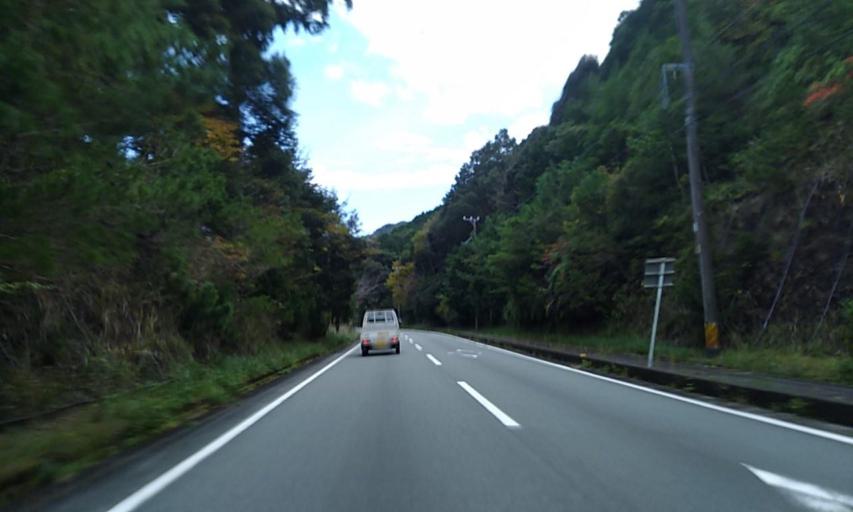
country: JP
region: Mie
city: Ise
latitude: 34.3003
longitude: 136.6077
